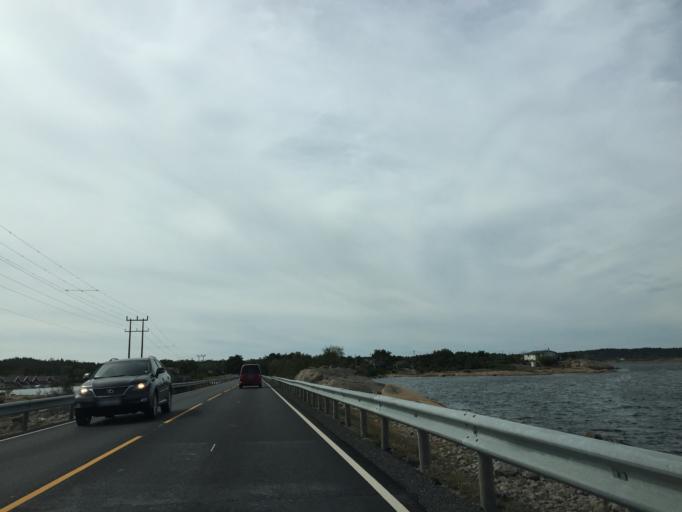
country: NO
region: Ostfold
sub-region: Fredrikstad
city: Fredrikstad
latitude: 59.1223
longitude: 10.9121
